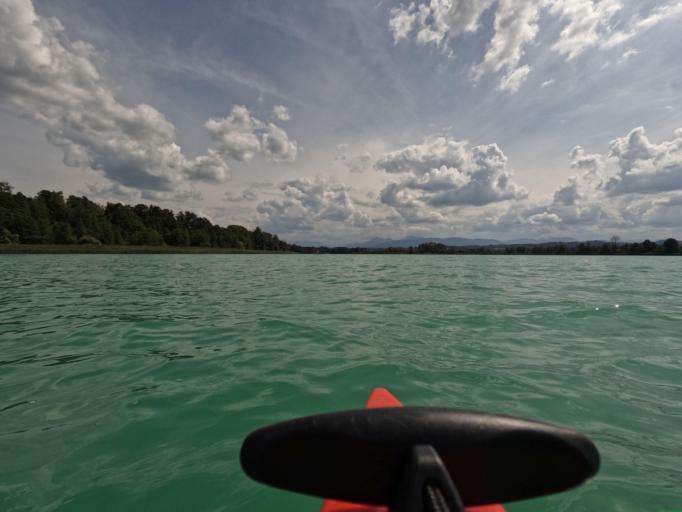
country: DE
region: Bavaria
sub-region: Upper Bavaria
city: Taching am See
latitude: 47.9624
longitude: 12.7430
